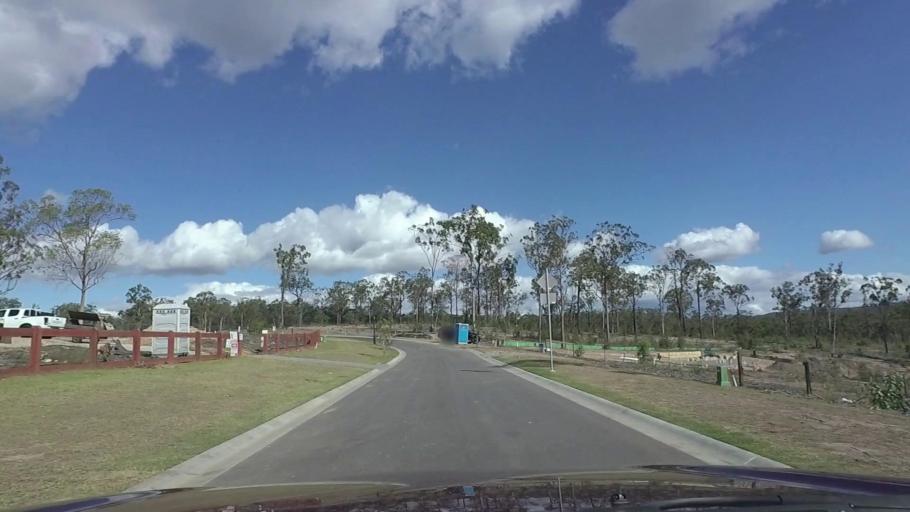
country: AU
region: Queensland
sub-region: Ipswich
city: Springfield Lakes
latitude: -27.7558
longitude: 152.9206
